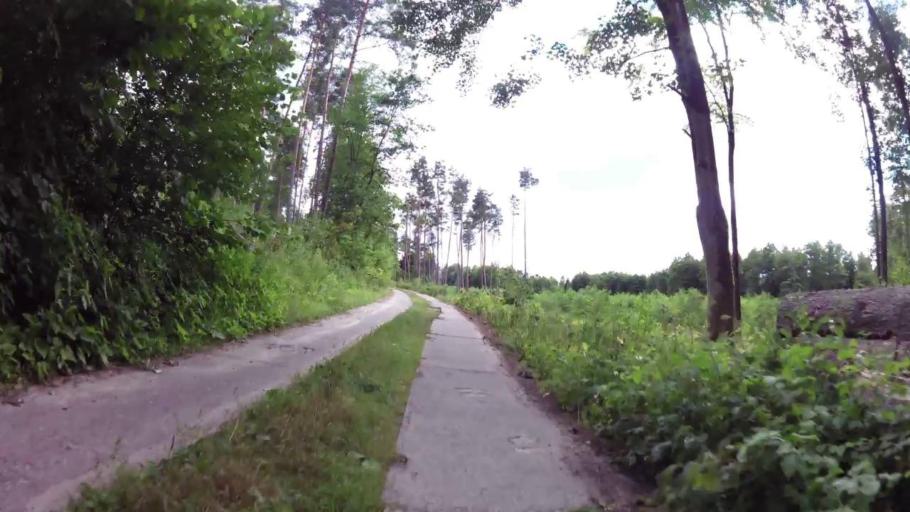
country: PL
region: West Pomeranian Voivodeship
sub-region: Powiat lobeski
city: Lobez
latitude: 53.6501
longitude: 15.5797
